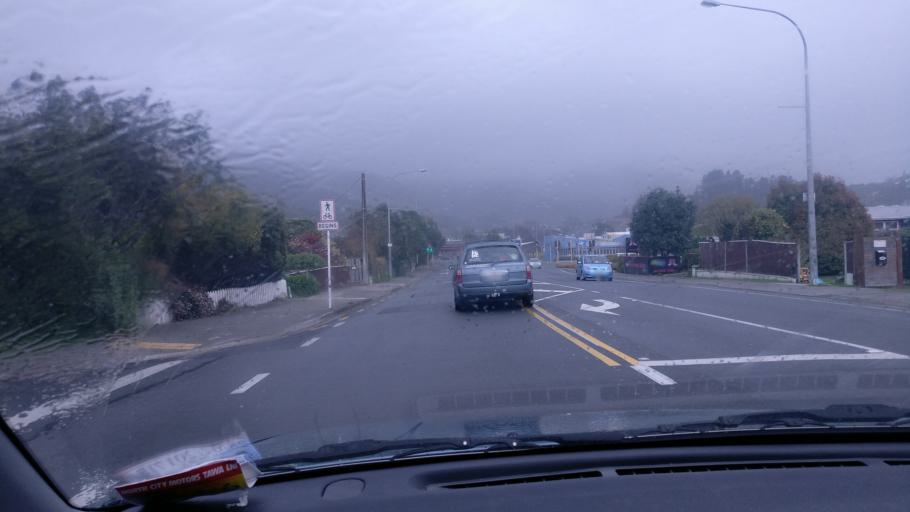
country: NZ
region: Wellington
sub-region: Kapiti Coast District
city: Paraparaumu
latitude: -40.9134
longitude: 175.0047
